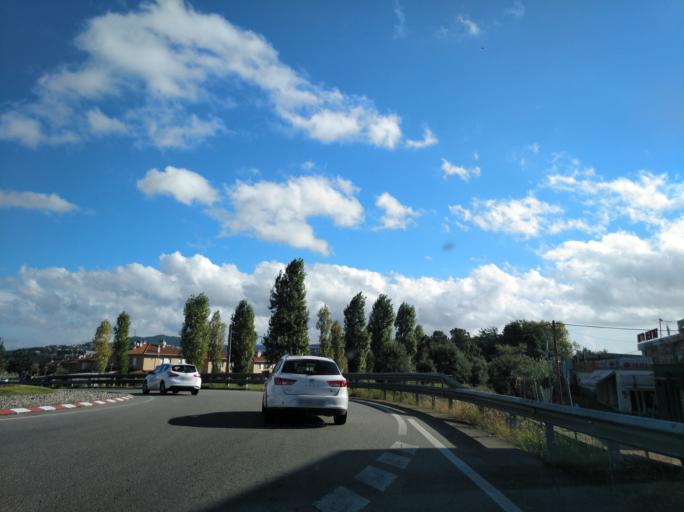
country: ES
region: Catalonia
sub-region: Provincia de Barcelona
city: Tordera
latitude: 41.6925
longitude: 2.7233
